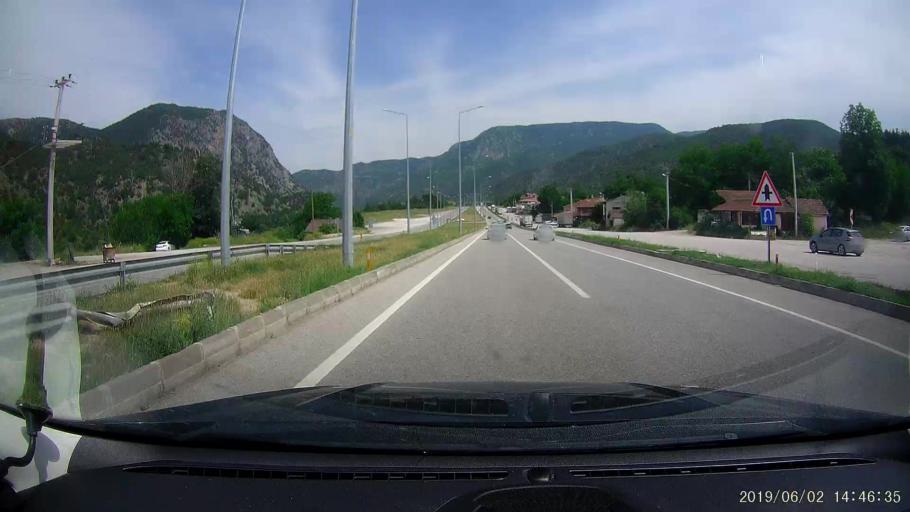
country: TR
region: Corum
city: Hacihamza
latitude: 41.0760
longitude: 34.4509
